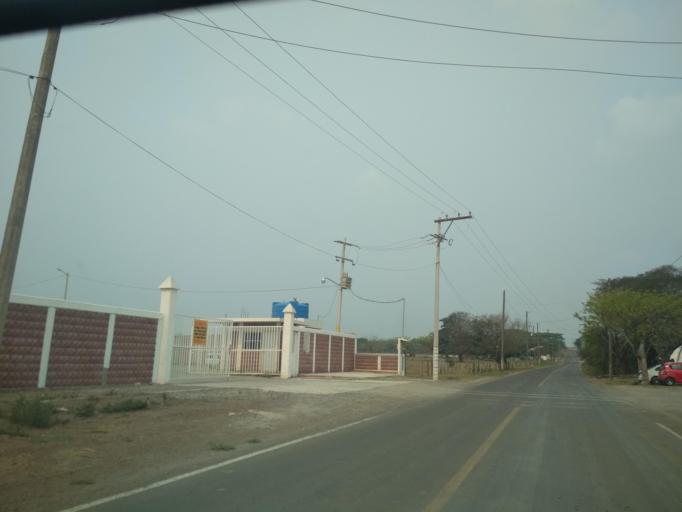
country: MX
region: Veracruz
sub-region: Veracruz
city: Delfino Victoria (Santa Fe)
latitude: 19.2100
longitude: -96.2527
